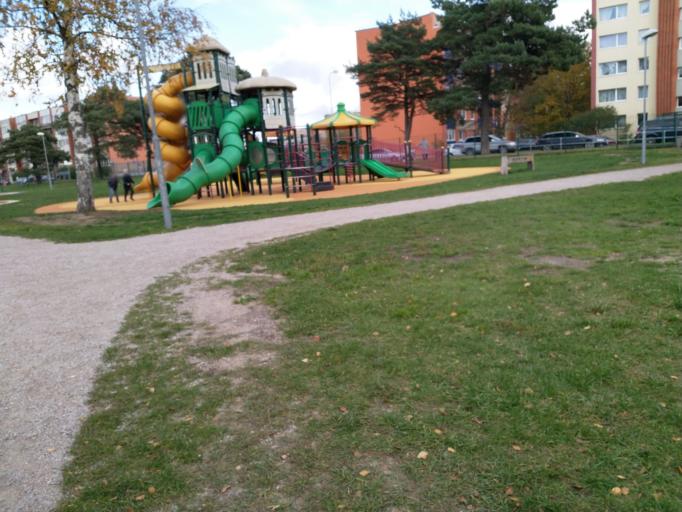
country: LV
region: Ventspils
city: Ventspils
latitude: 57.4080
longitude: 21.5928
